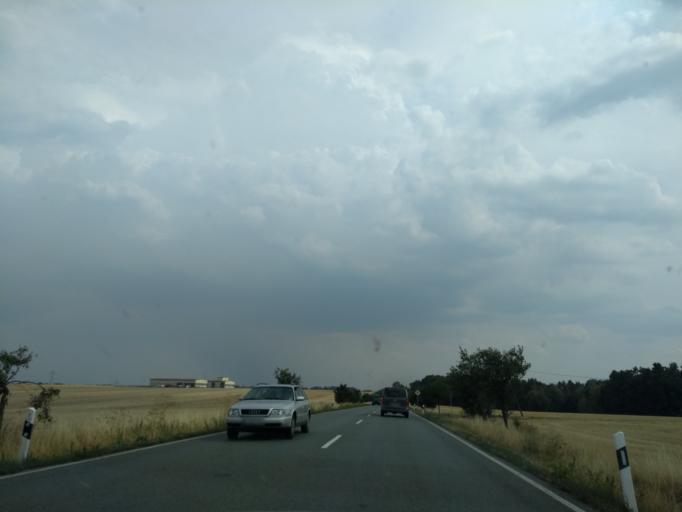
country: DE
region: Saxony-Anhalt
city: Zeitz
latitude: 50.9965
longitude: 12.1339
